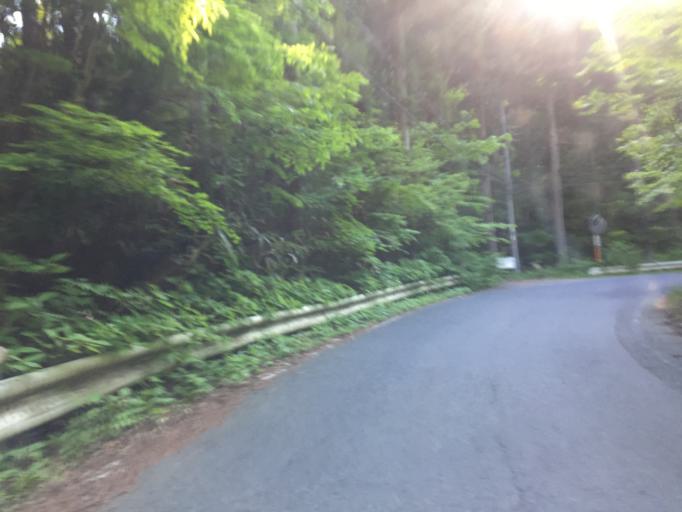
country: JP
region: Ibaraki
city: Kitaibaraki
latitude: 36.8612
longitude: 140.6381
